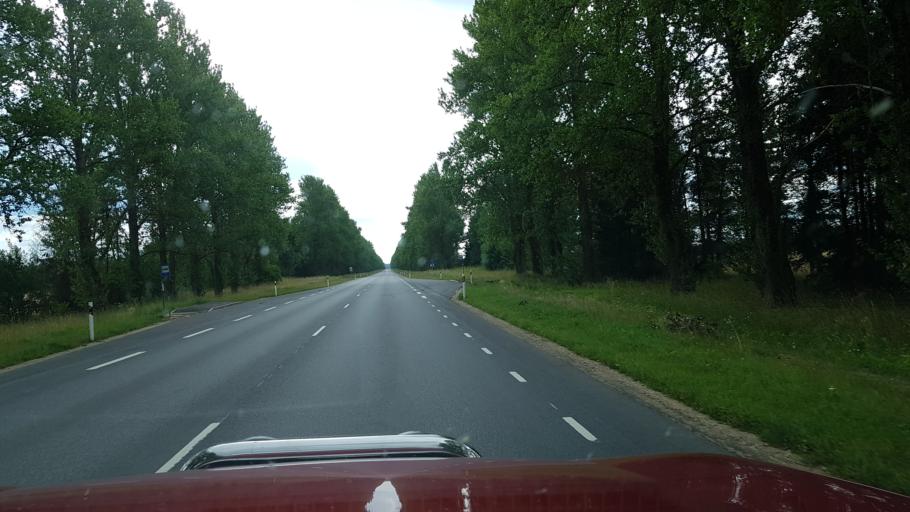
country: EE
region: Polvamaa
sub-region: Polva linn
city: Polva
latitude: 58.3001
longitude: 27.0012
